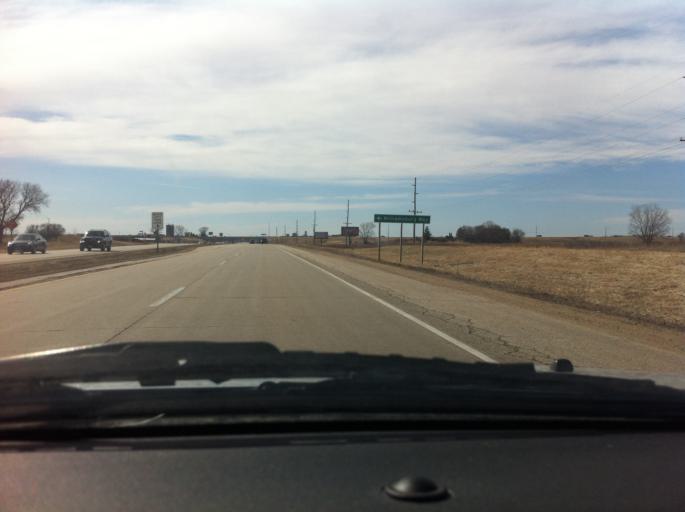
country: US
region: Wisconsin
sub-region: Dane County
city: Windsor
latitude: 43.1947
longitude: -89.3136
